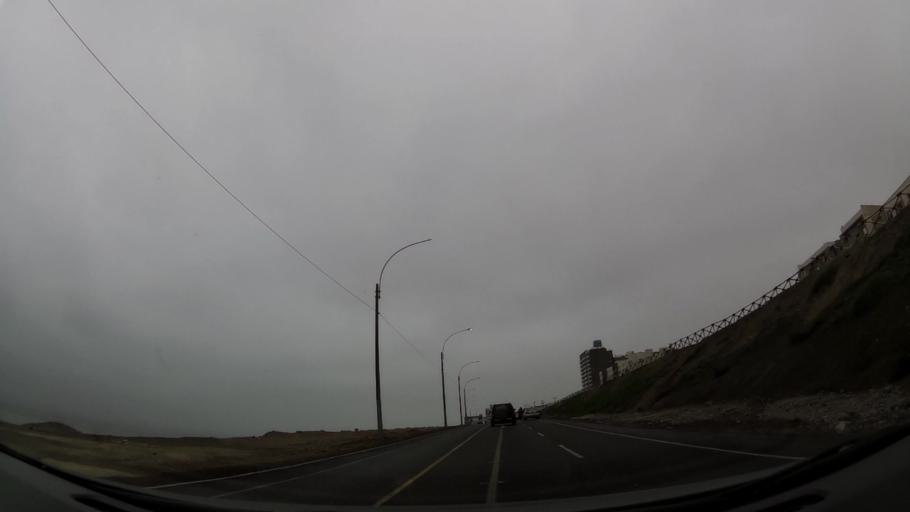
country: PE
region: Callao
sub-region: Callao
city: Callao
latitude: -12.0880
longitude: -77.0924
